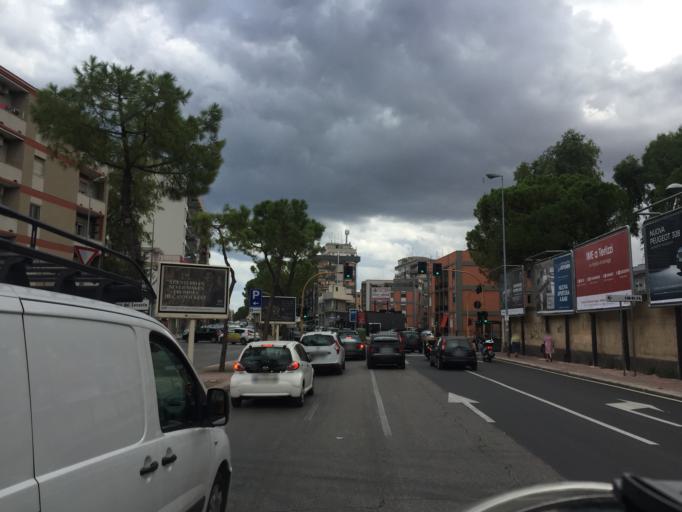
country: IT
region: Apulia
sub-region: Provincia di Bari
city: Bari
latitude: 41.1073
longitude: 16.8592
